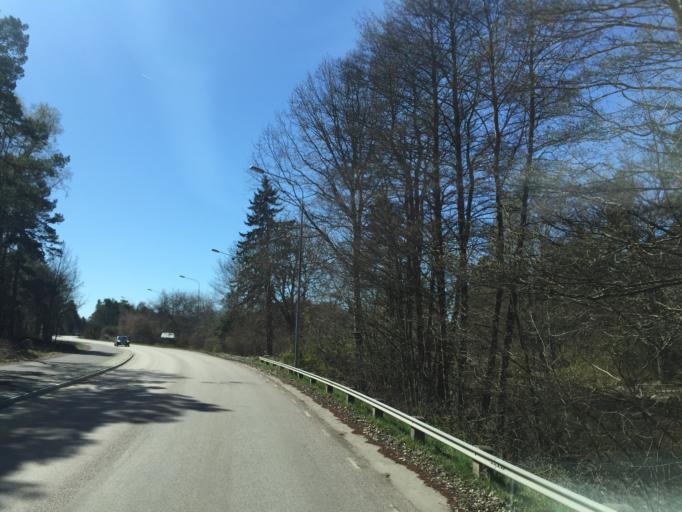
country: SE
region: Kalmar
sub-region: Oskarshamns Kommun
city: Oskarshamn
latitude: 57.2526
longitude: 16.4609
